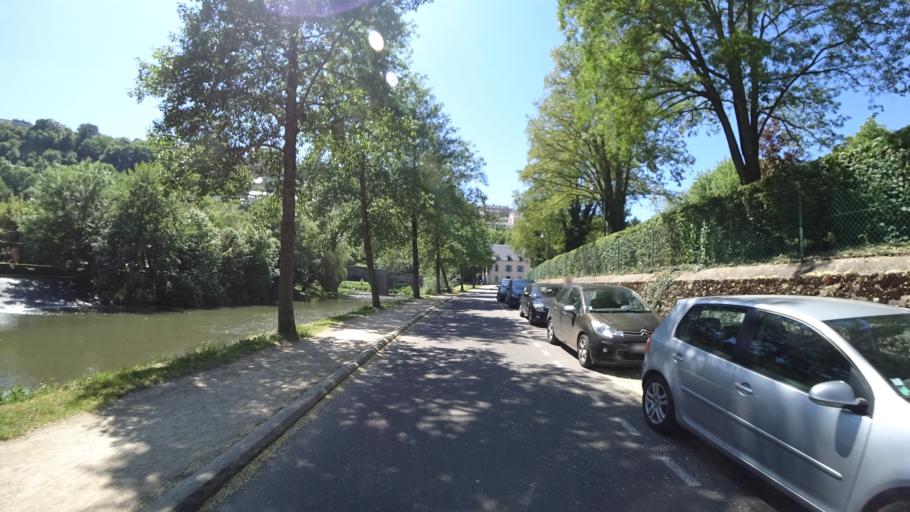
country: FR
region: Midi-Pyrenees
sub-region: Departement de l'Aveyron
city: Rodez
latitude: 44.3535
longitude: 2.5823
